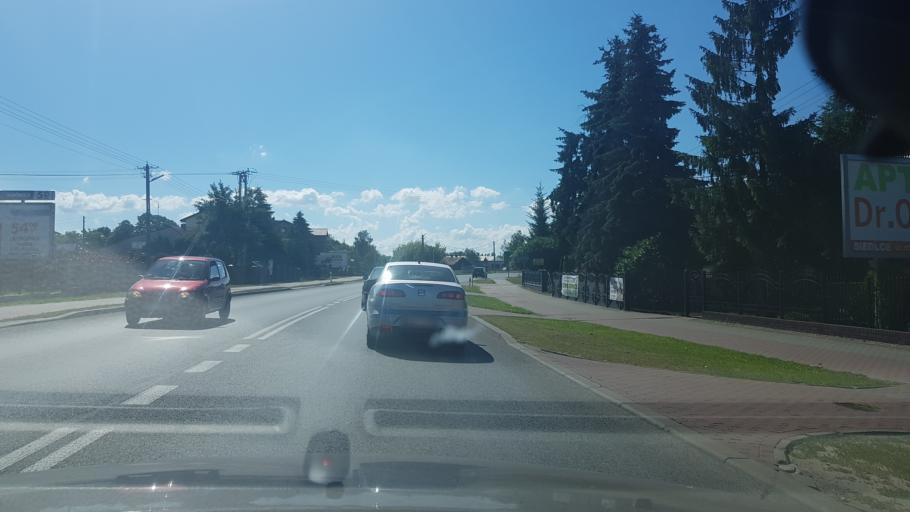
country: PL
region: Masovian Voivodeship
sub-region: Siedlce
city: Siedlce
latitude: 52.1972
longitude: 22.2628
